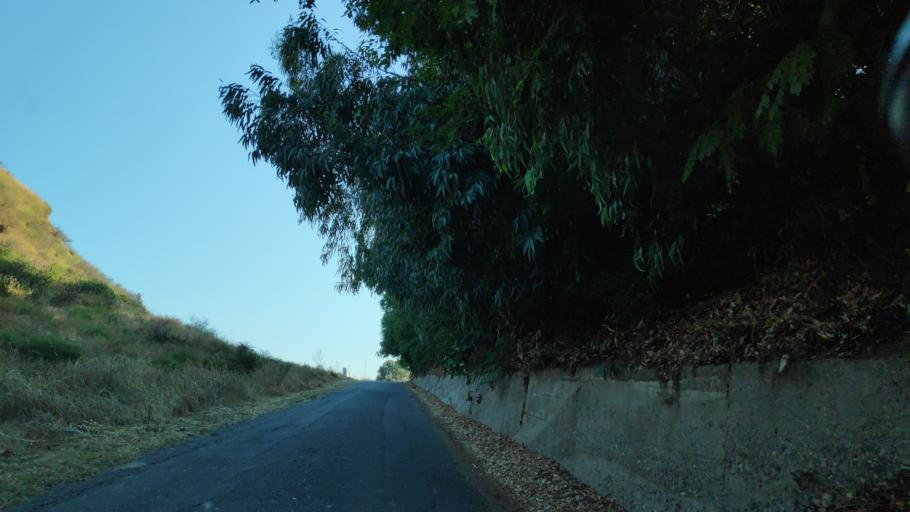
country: IT
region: Calabria
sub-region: Provincia di Reggio Calabria
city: Monasterace Marina
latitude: 38.4488
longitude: 16.5713
